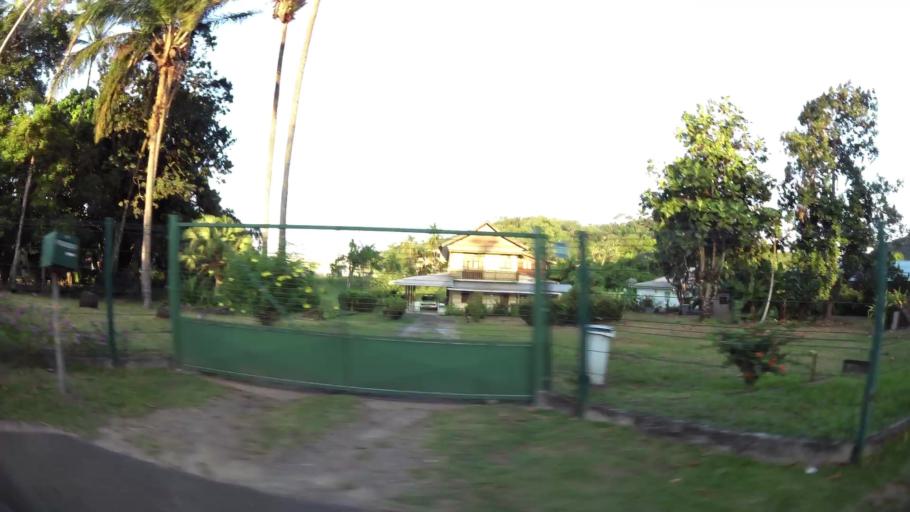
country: GF
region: Guyane
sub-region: Guyane
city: Cayenne
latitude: 4.9250
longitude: -52.3036
